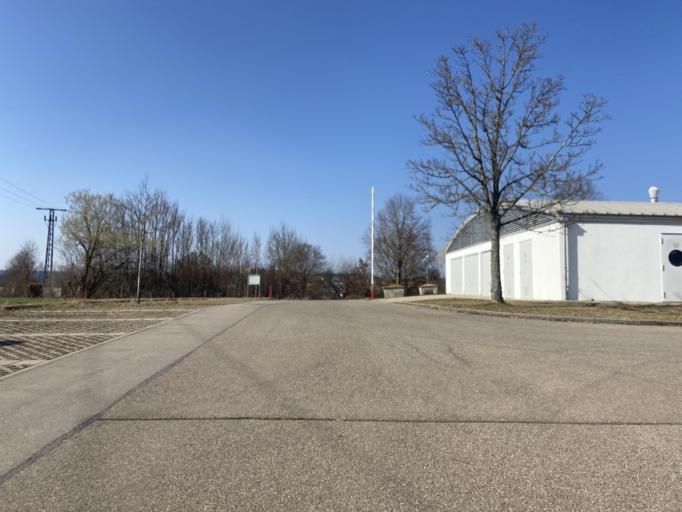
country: DE
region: Baden-Wuerttemberg
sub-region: Tuebingen Region
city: Sigmaringen
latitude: 48.0860
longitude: 9.2370
